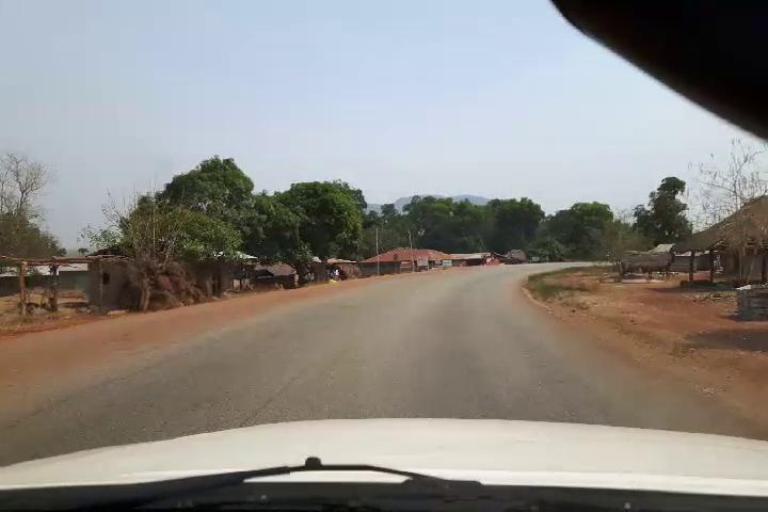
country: SL
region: Northern Province
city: Yonibana
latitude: 8.3994
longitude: -12.1950
